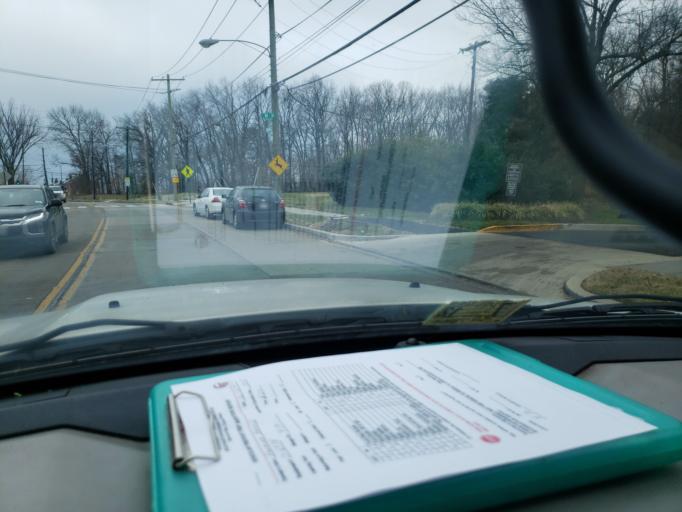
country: US
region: Maryland
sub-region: Prince George's County
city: Capitol Heights
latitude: 38.8883
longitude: -76.9403
